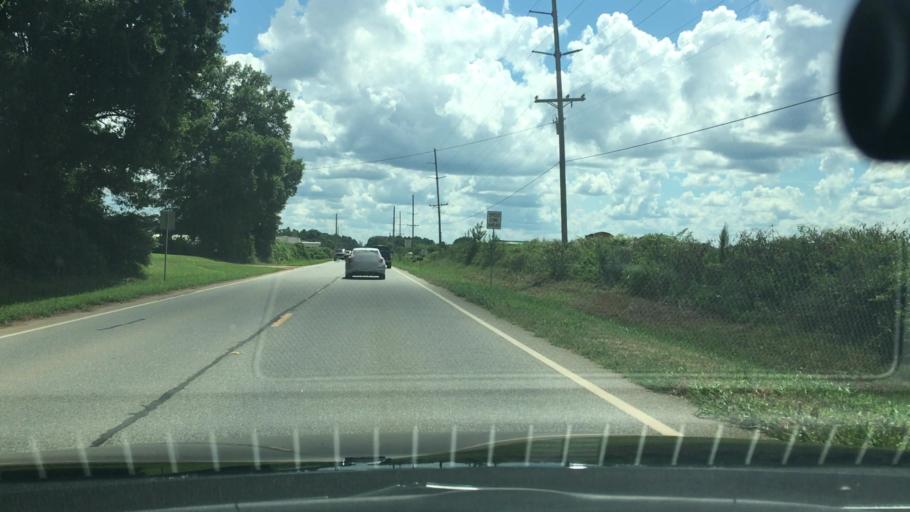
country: US
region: Georgia
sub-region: Putnam County
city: Eatonton
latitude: 33.3495
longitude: -83.3547
